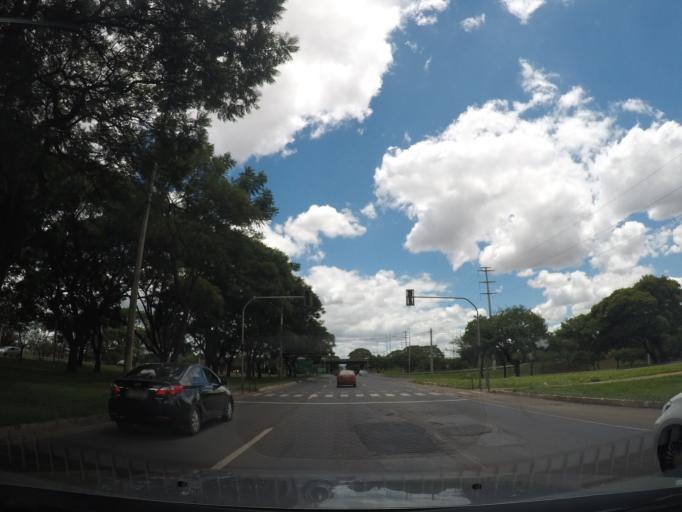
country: BR
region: Federal District
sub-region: Brasilia
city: Brasilia
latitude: -15.8082
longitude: -47.9484
